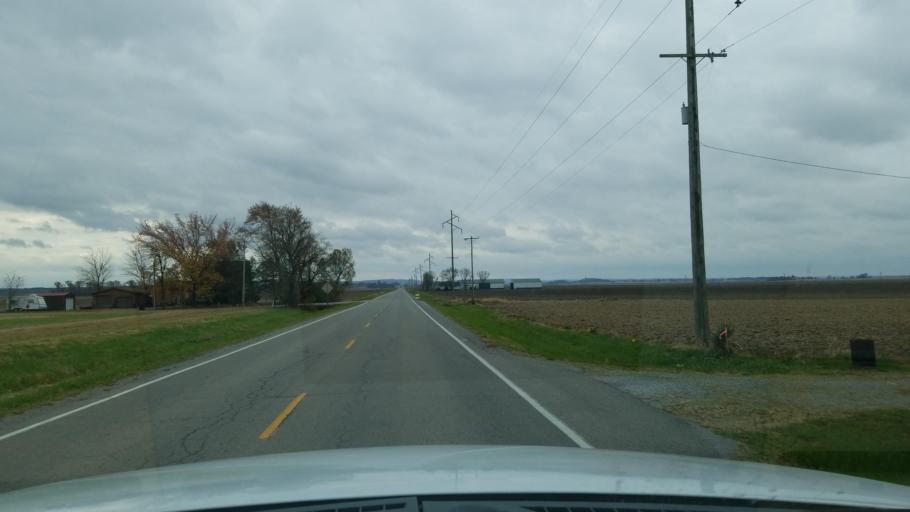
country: US
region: Illinois
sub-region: Saline County
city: Eldorado
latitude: 37.7878
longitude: -88.4382
